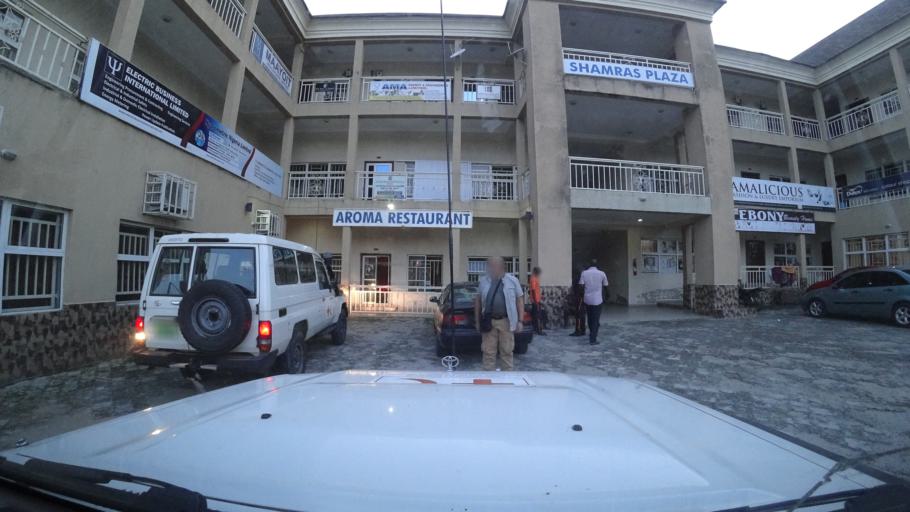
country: NG
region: Niger
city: Minna
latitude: 9.6341
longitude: 6.5429
